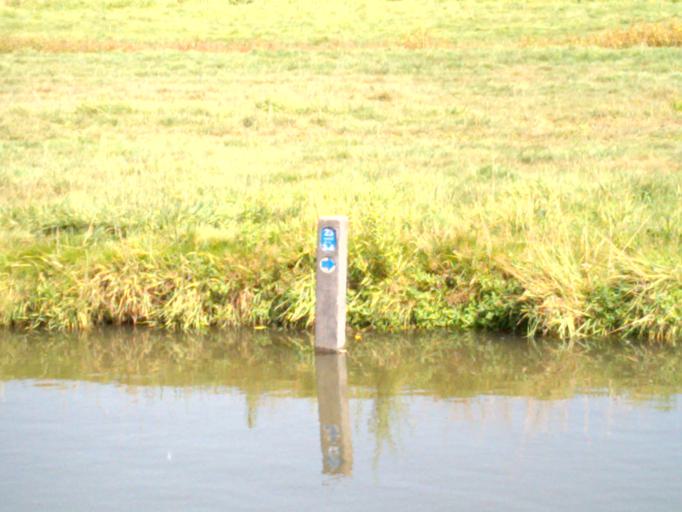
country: NL
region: North Holland
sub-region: Gemeente Alkmaar
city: Alkmaar
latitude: 52.5779
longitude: 4.8081
